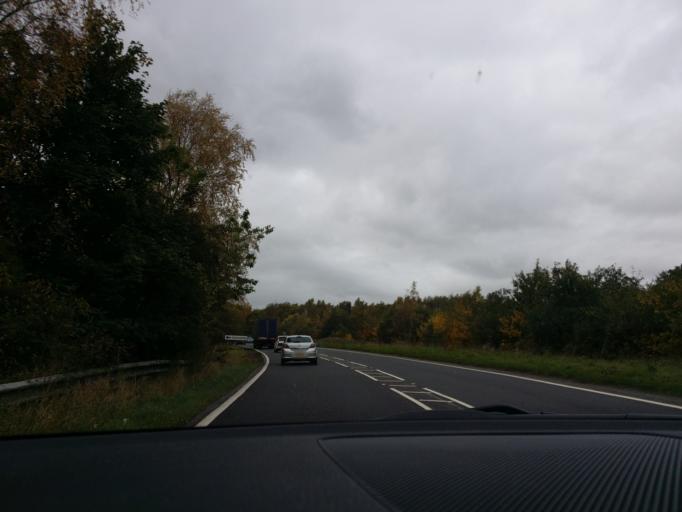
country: GB
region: Scotland
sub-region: Clackmannanshire
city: Clackmannan
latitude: 56.1122
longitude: -3.7460
